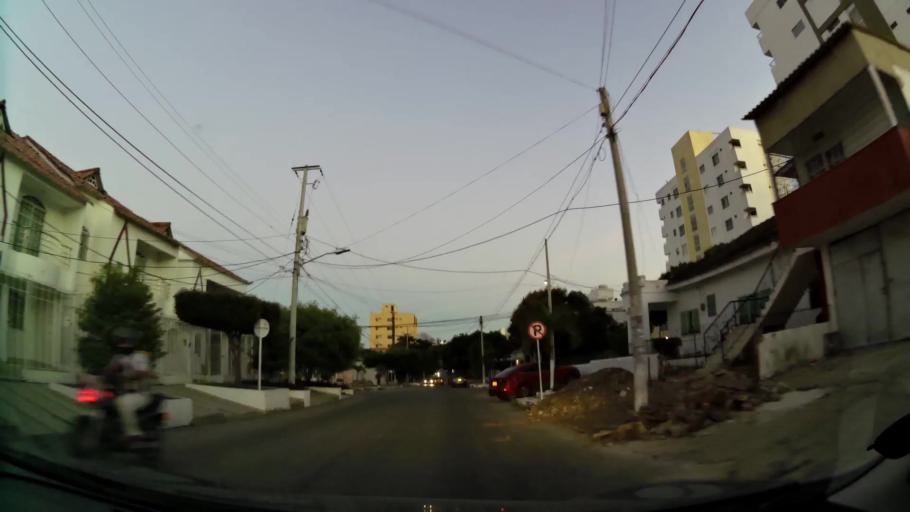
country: CO
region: Atlantico
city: Barranquilla
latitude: 10.9878
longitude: -74.8022
